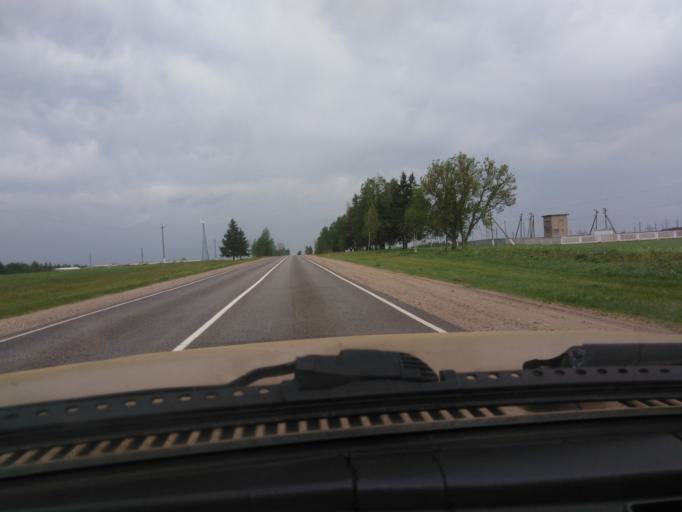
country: BY
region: Mogilev
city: Palykavichy Pyershyya
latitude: 54.0132
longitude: 30.3213
